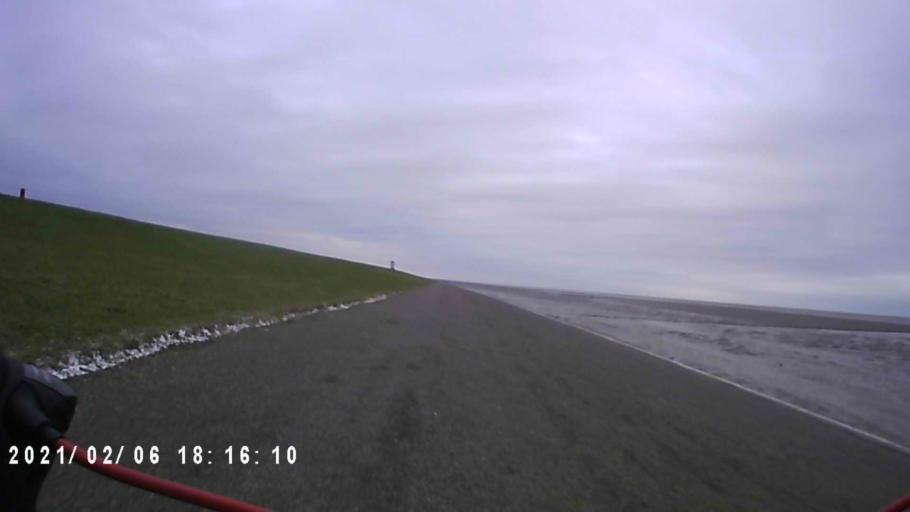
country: DE
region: Lower Saxony
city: Borkum
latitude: 53.4656
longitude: 6.7489
